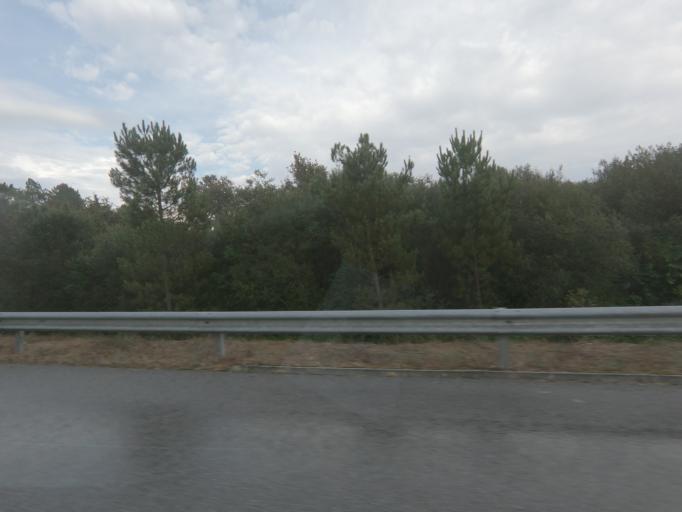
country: PT
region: Viseu
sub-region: Viseu
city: Campo
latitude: 40.7216
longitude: -7.9238
